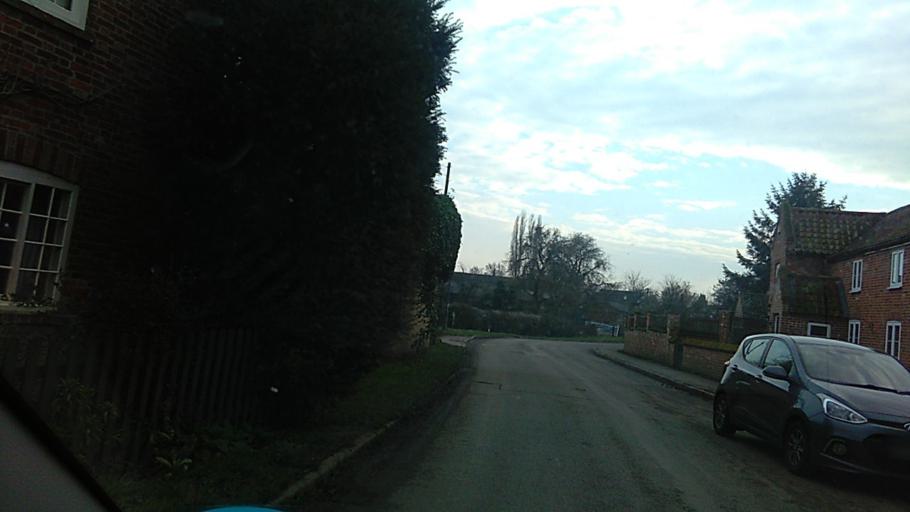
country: GB
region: England
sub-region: Nottinghamshire
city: Cropwell Bishop
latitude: 52.8566
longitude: -0.9749
